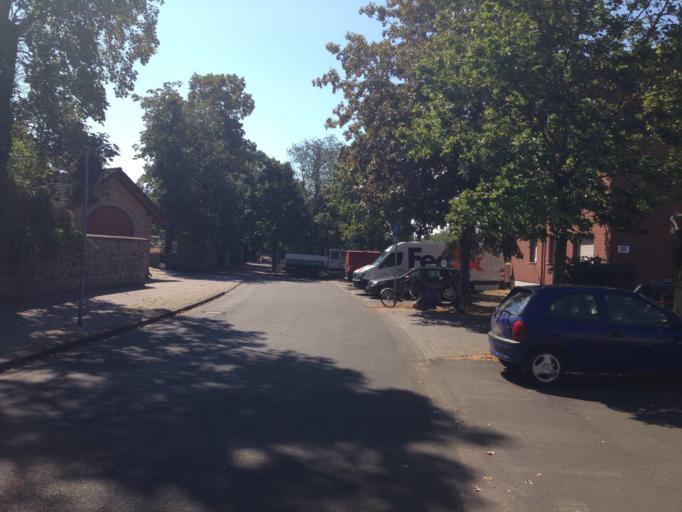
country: DE
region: Hesse
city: Lollar
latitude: 50.6429
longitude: 8.7025
